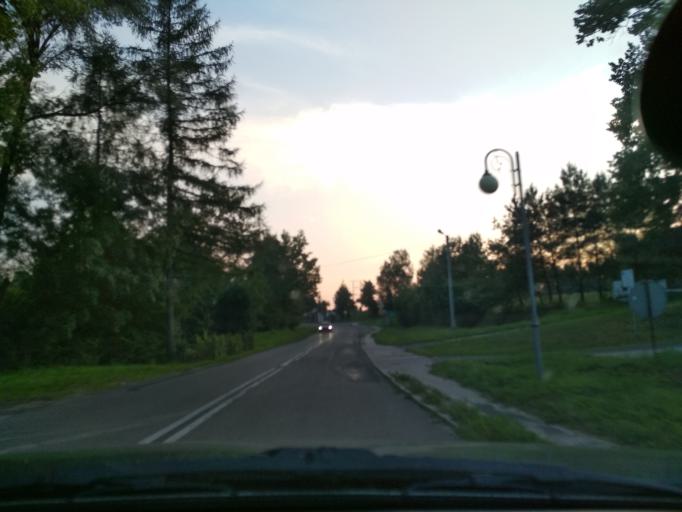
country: PL
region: Lesser Poland Voivodeship
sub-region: Powiat olkuski
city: Wolbrom
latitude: 50.4453
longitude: 19.8187
